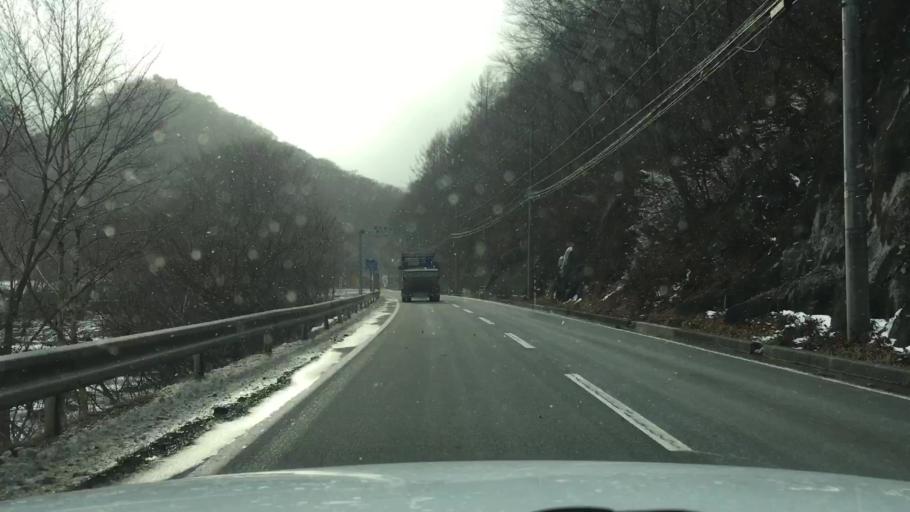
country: JP
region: Iwate
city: Tono
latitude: 39.6186
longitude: 141.4920
